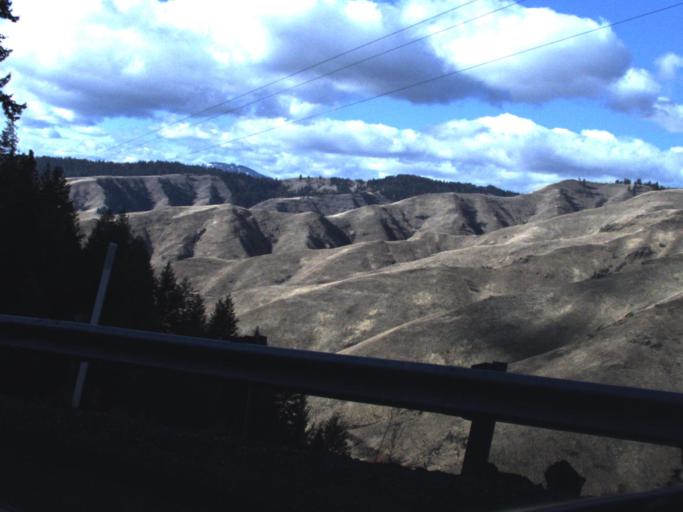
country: US
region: Washington
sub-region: Asotin County
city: Asotin
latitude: 46.0781
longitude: -117.2011
